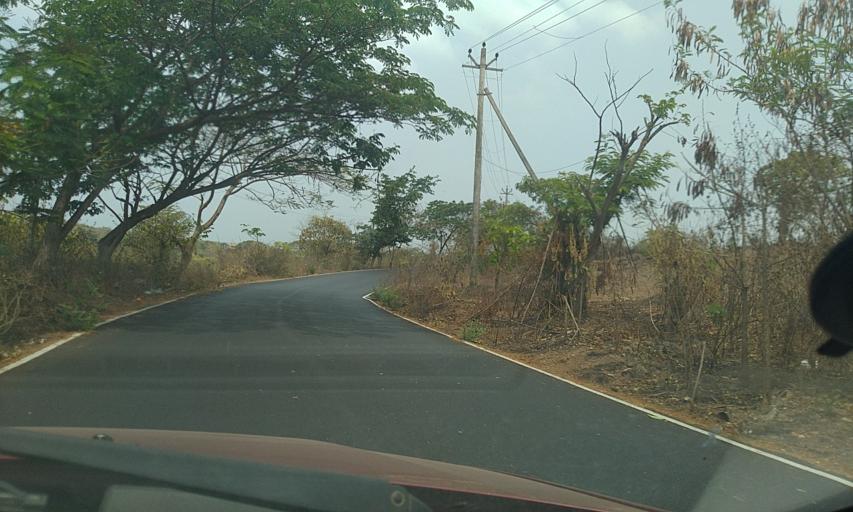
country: IN
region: Goa
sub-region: North Goa
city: Mapuca
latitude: 15.6067
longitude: 73.8016
